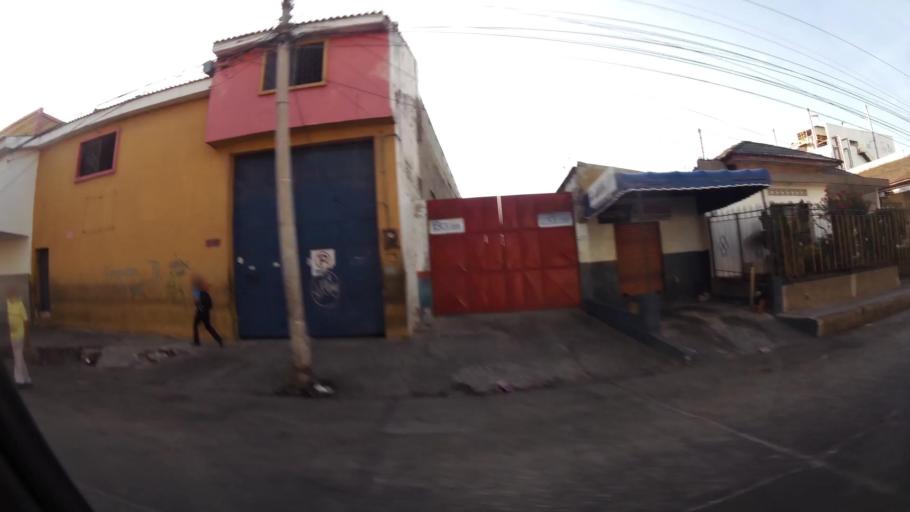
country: CO
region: Atlantico
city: Barranquilla
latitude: 10.9848
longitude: -74.7905
